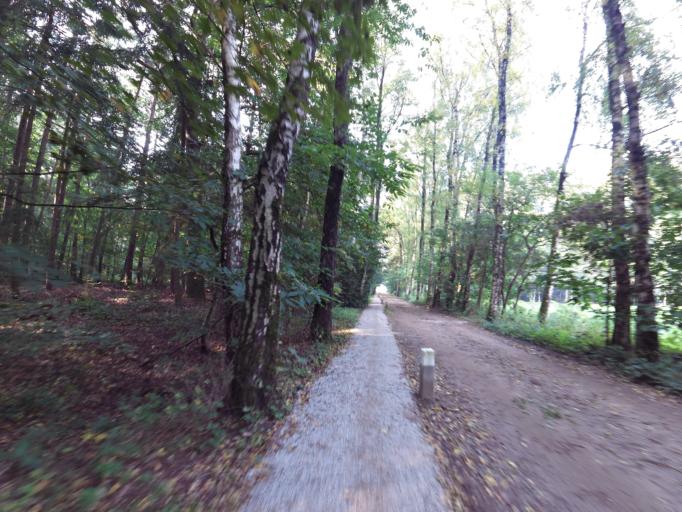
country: NL
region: Gelderland
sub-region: Gemeente Doesburg
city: Doesburg
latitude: 51.9530
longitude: 6.1840
